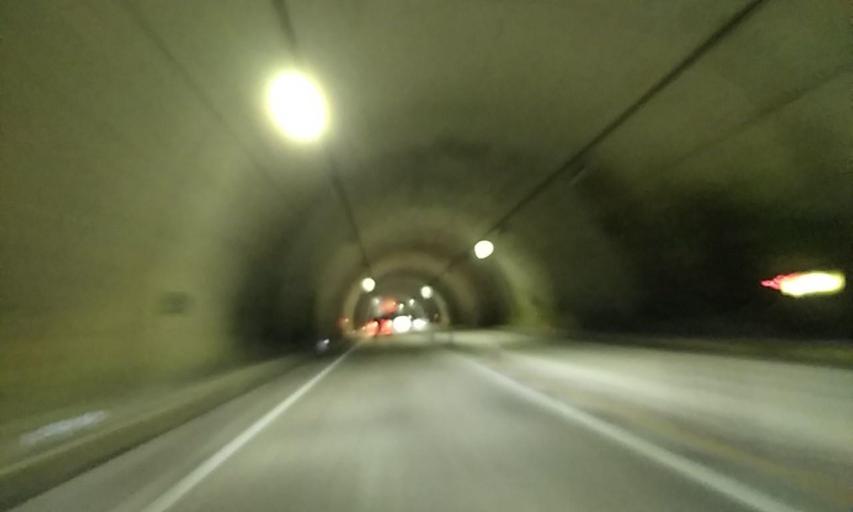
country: JP
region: Wakayama
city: Shingu
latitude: 33.7206
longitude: 135.9747
